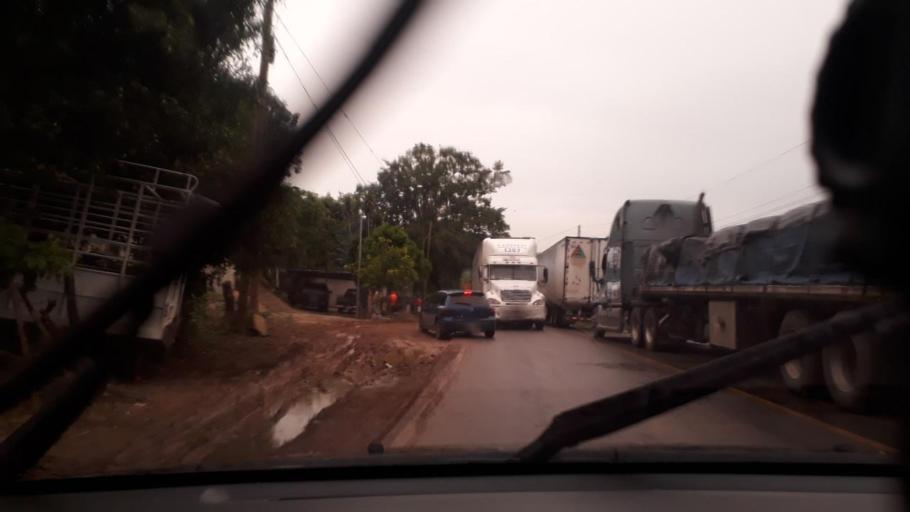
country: GT
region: Jutiapa
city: Atescatempa
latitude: 14.2031
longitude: -89.6807
